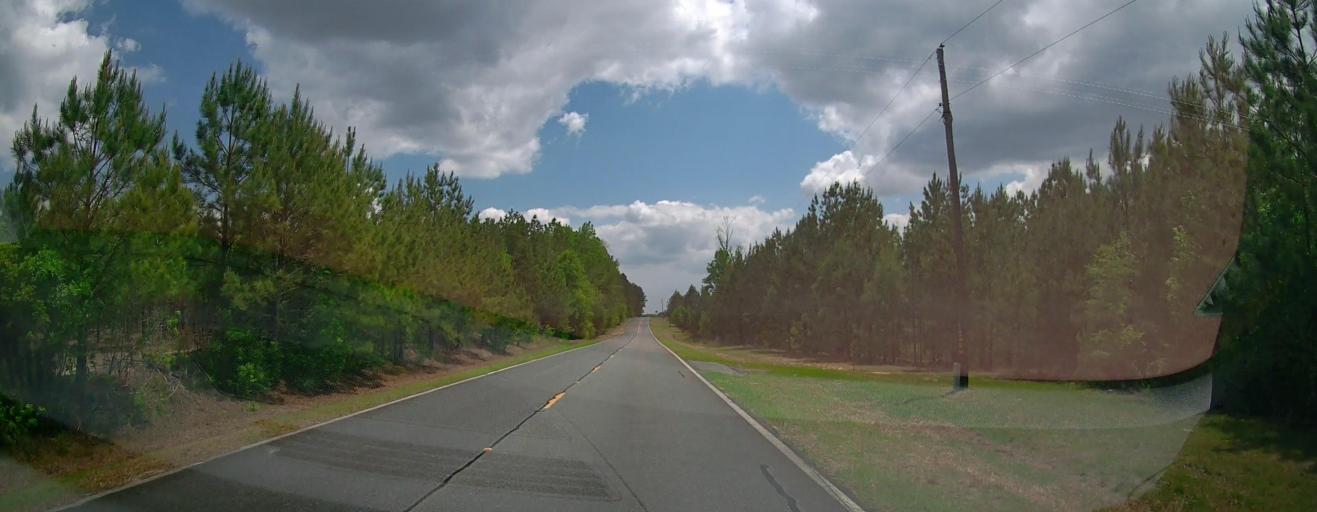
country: US
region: Georgia
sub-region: Treutlen County
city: Soperton
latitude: 32.4896
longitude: -82.6050
